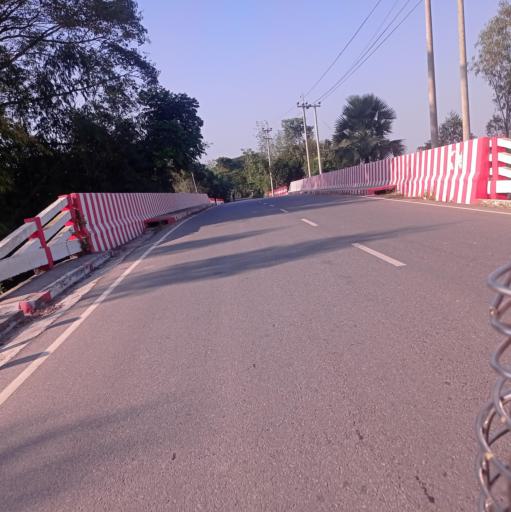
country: BD
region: Dhaka
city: Bajitpur
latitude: 24.1430
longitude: 90.8164
